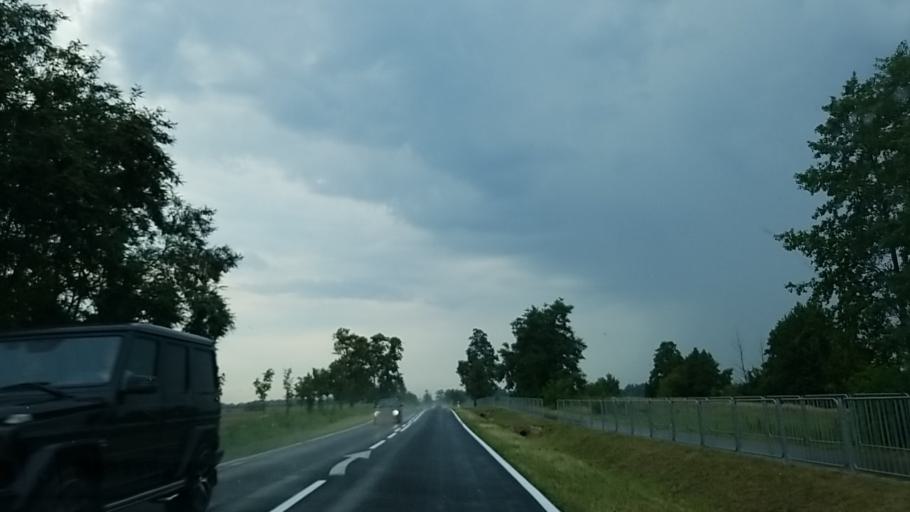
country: PL
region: Lublin Voivodeship
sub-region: Powiat wlodawski
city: Wlodawa
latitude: 51.5968
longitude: 23.5353
